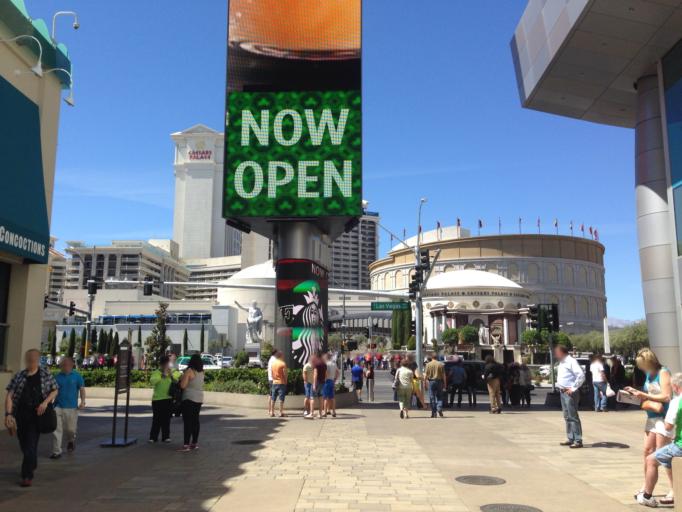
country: US
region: Nevada
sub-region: Clark County
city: Paradise
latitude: 36.1175
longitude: -115.1724
